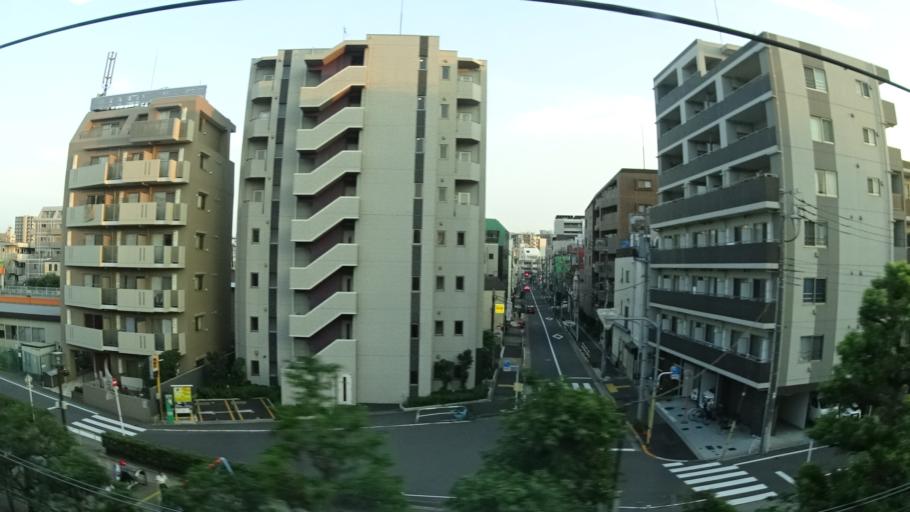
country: JP
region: Saitama
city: Soka
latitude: 35.7335
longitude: 139.7756
